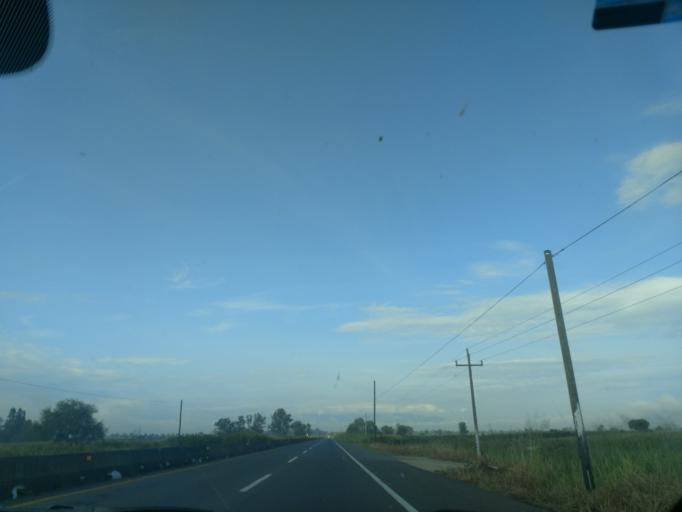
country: MX
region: Jalisco
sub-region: Ameca
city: Los Pocitos
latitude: 20.5450
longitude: -103.9113
